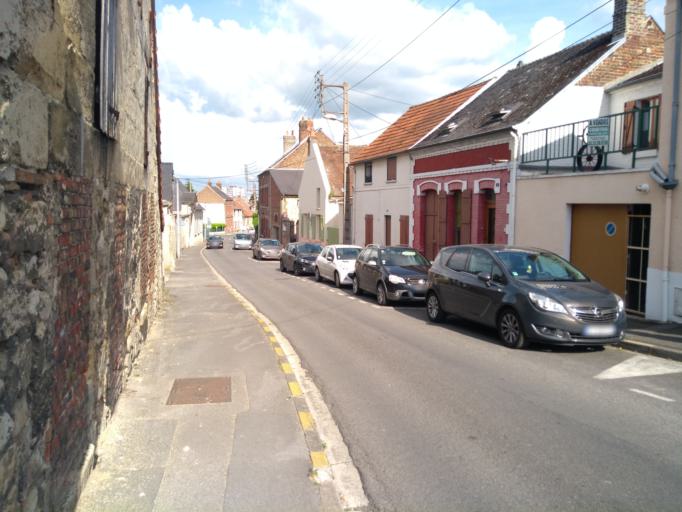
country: FR
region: Picardie
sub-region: Departement de l'Aisne
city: Laon
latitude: 49.5676
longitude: 3.6344
